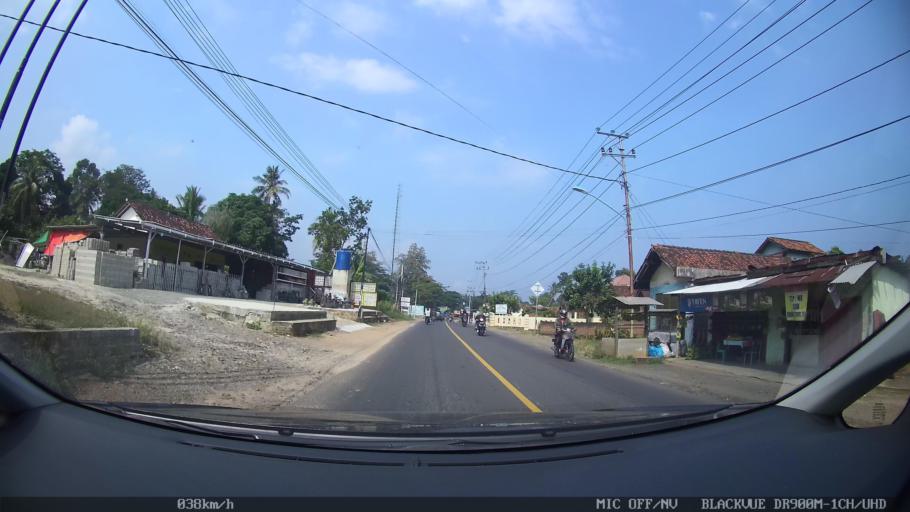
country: ID
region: Lampung
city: Natar
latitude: -5.3685
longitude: 105.1776
